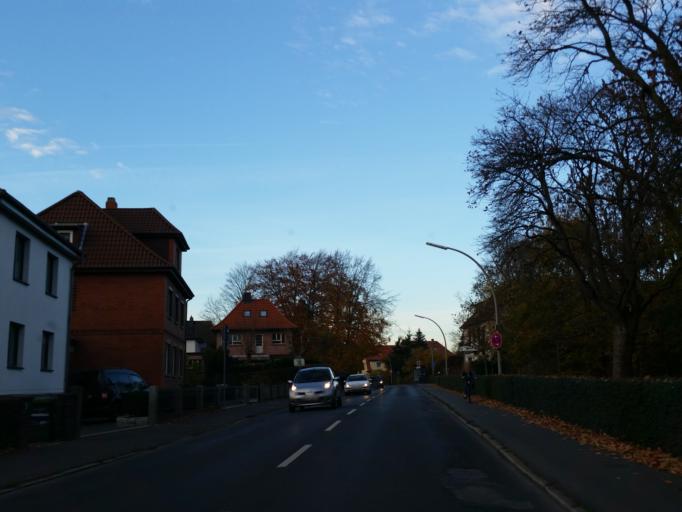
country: DE
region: Lower Saxony
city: Braunschweig
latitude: 52.2743
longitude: 10.5701
